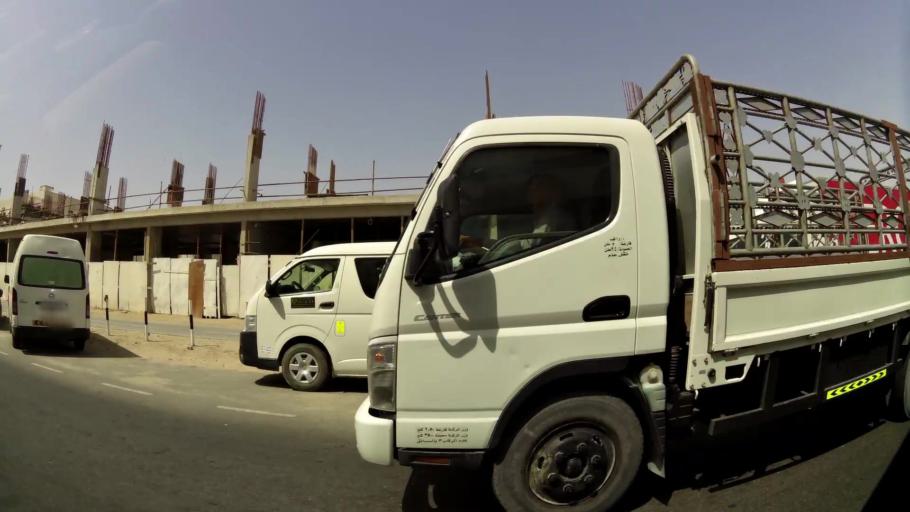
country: AE
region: Dubai
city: Dubai
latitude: 25.1573
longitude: 55.2500
